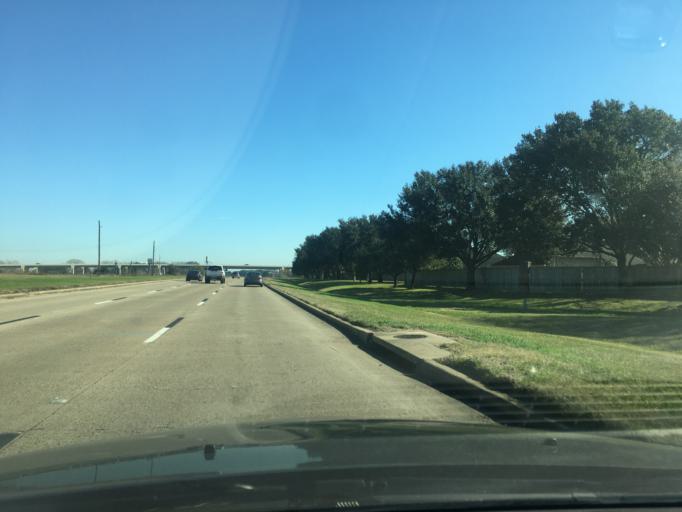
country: US
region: Texas
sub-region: Fort Bend County
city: New Territory
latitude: 29.6010
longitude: -95.6906
